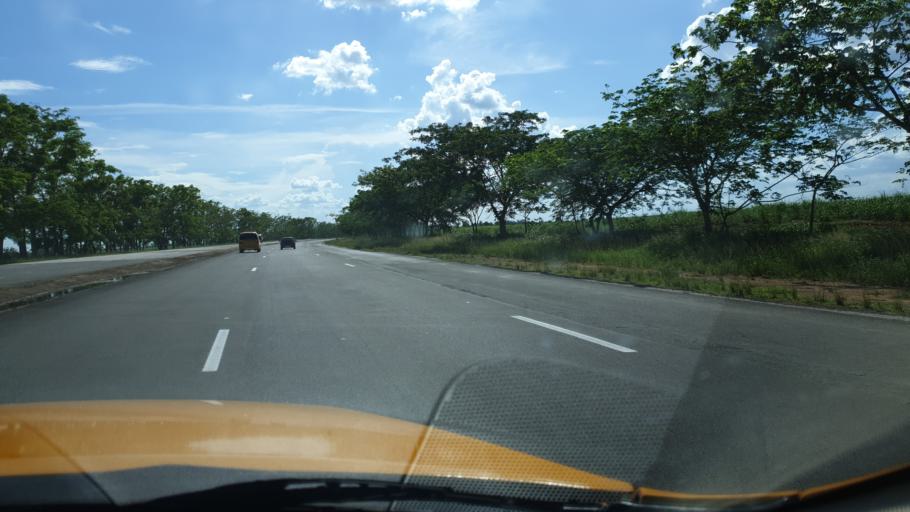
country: CU
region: Cienfuegos
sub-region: Municipio de Aguada de Pasajeros
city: Aguada de Pasajeros
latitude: 22.4022
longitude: -80.8506
